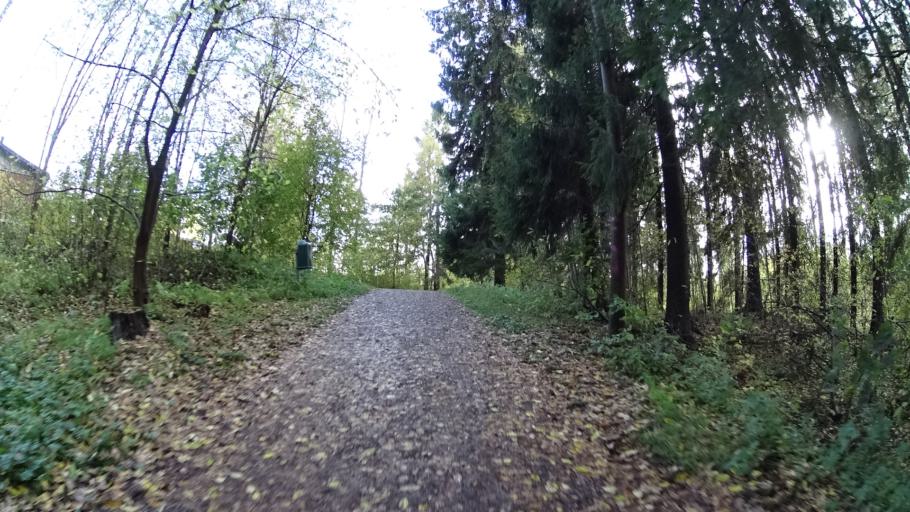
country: FI
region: Uusimaa
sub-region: Helsinki
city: Kilo
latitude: 60.2704
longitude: 24.8173
